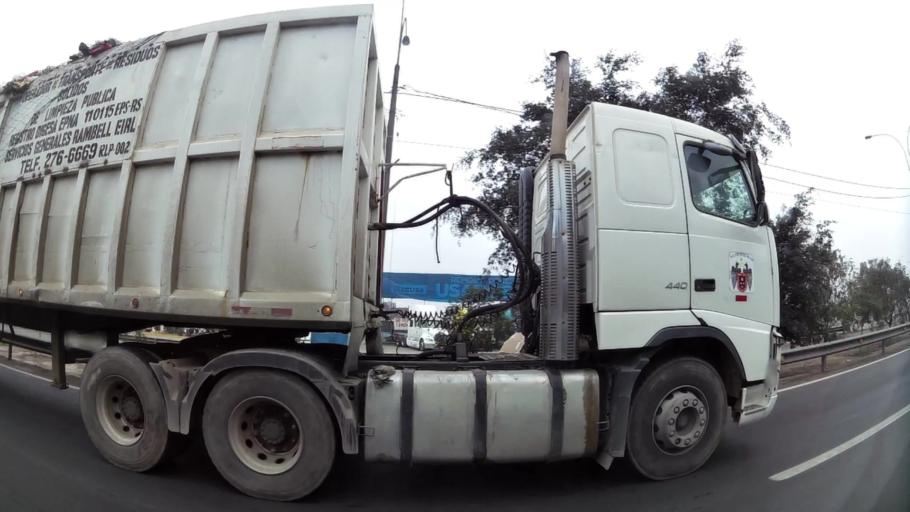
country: PE
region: Lima
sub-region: Lima
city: Vitarte
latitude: -12.0208
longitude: -76.9351
